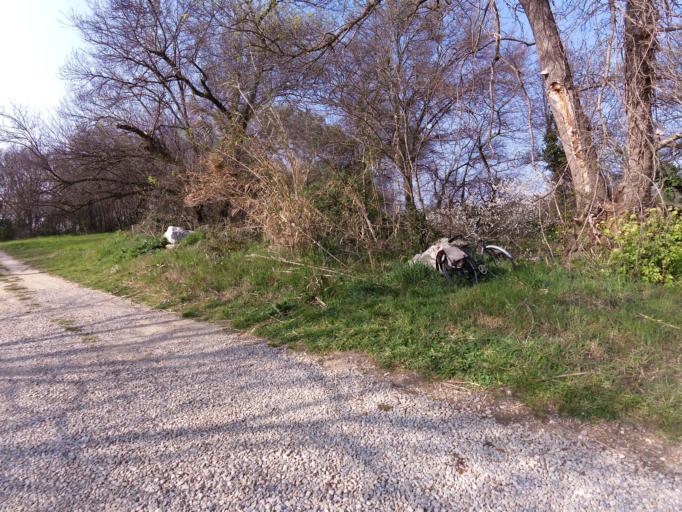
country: FR
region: Languedoc-Roussillon
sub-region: Departement du Gard
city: Vestric-et-Candiac
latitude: 43.7287
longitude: 4.2648
